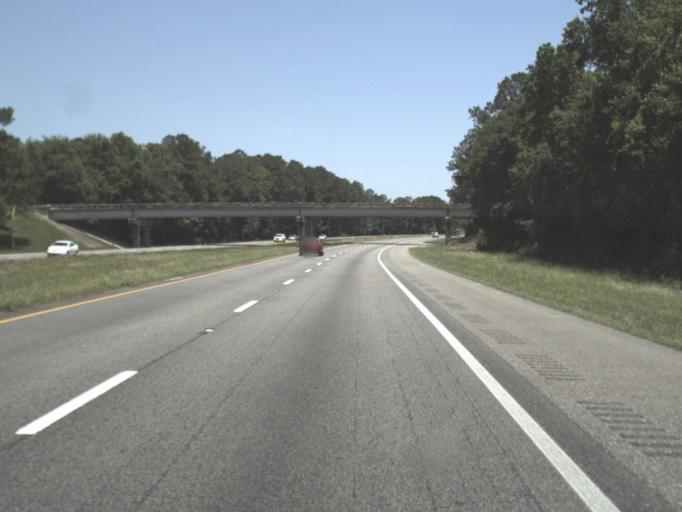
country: US
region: Florida
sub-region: Jefferson County
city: Monticello
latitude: 30.4724
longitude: -83.8253
